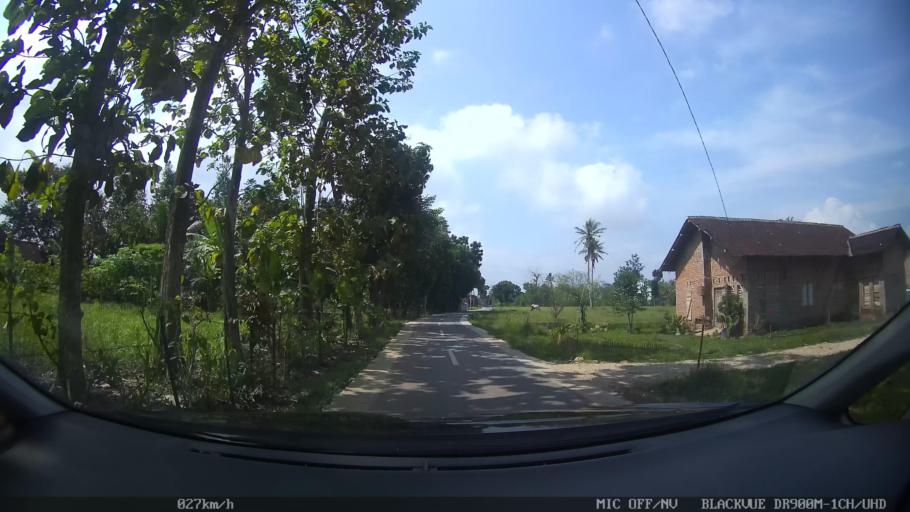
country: ID
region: Lampung
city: Kedaton
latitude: -5.3321
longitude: 105.2726
